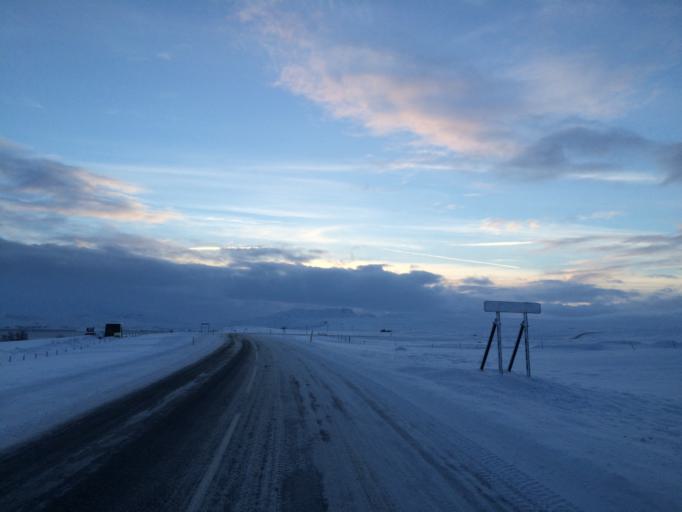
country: IS
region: South
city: Hveragerdi
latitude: 64.2328
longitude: -21.1975
